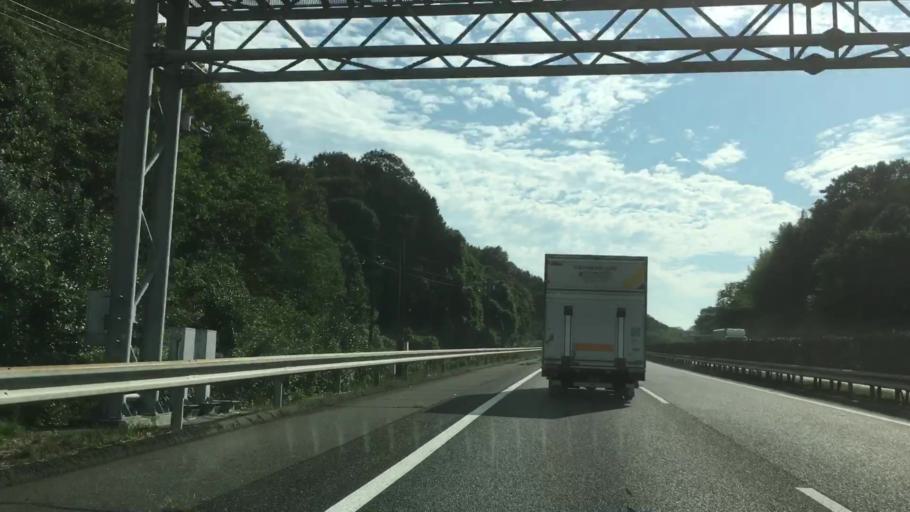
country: JP
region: Yamaguchi
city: Yanai
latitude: 34.0742
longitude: 132.0679
